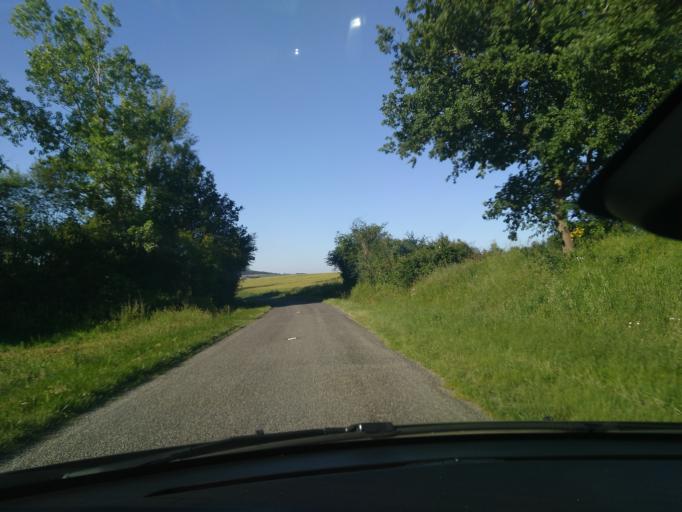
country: FR
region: Midi-Pyrenees
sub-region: Departement du Tarn-et-Garonne
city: Beaumont-de-Lomagne
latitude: 43.8441
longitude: 1.0733
